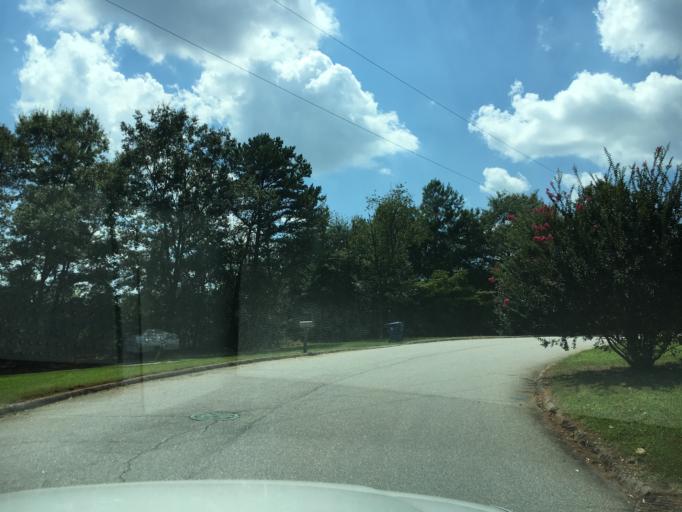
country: US
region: South Carolina
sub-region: Spartanburg County
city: Duncan
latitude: 34.9287
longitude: -82.1360
